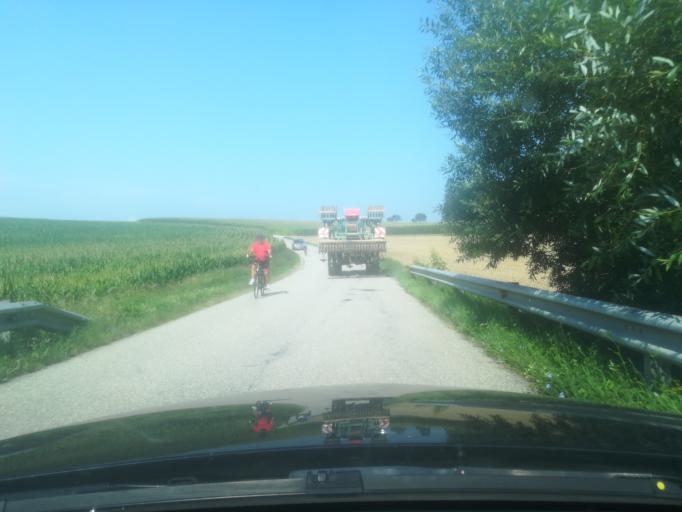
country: AT
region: Upper Austria
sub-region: Wels-Land
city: Holzhausen
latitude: 48.2177
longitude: 14.0721
